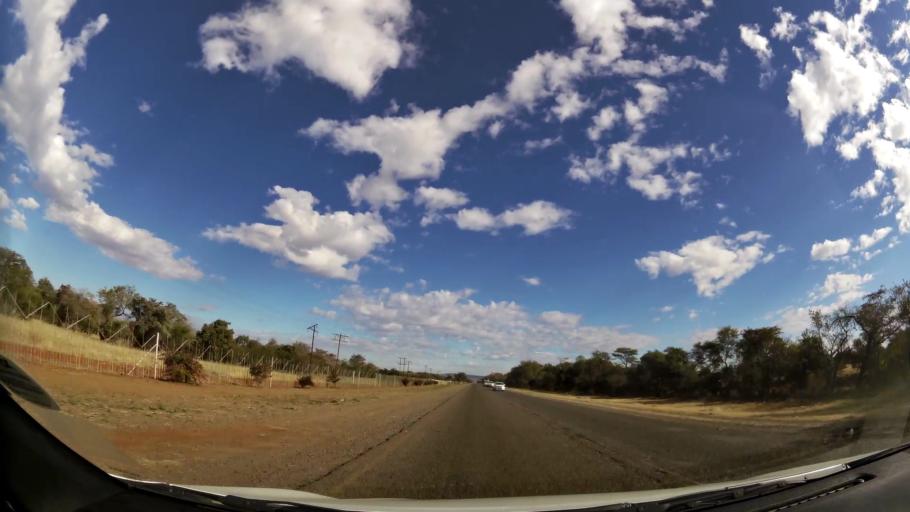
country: ZA
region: Limpopo
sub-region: Waterberg District Municipality
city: Bela-Bela
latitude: -24.9122
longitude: 28.3566
